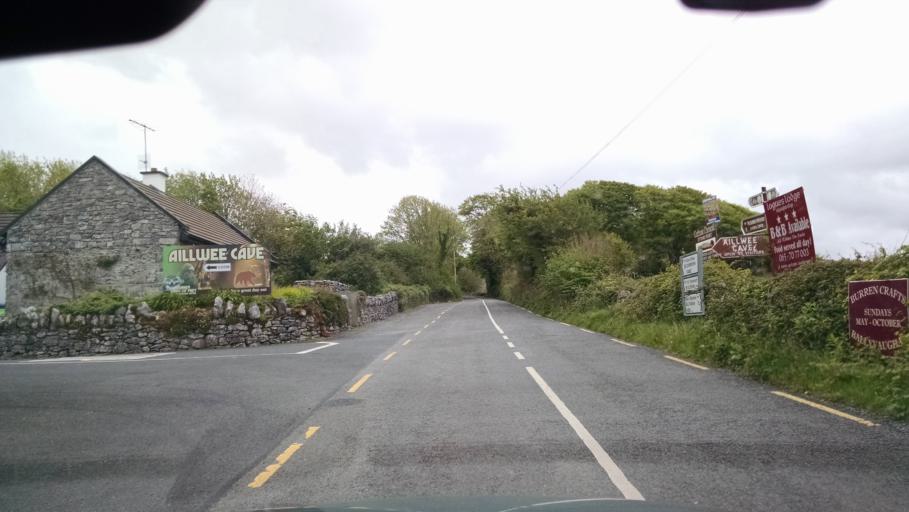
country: IE
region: Connaught
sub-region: County Galway
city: Bearna
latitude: 53.0915
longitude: -9.1584
